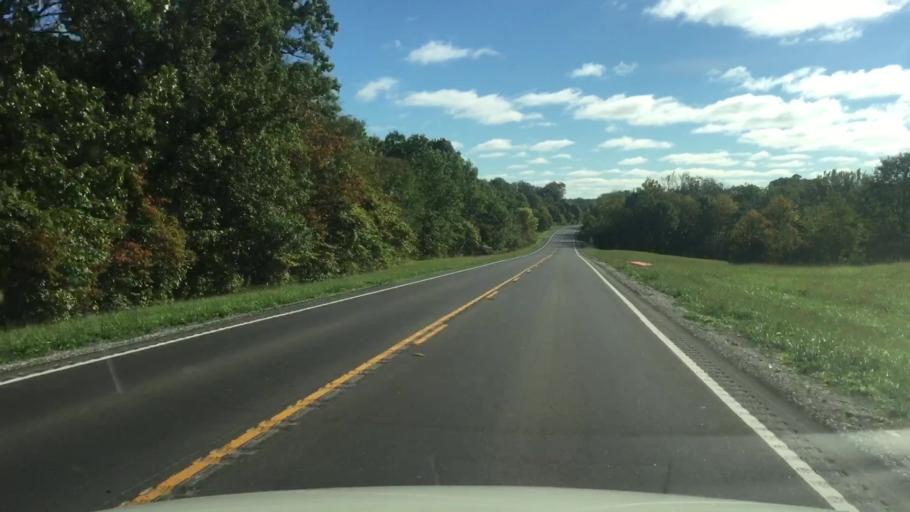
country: US
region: Missouri
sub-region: Howard County
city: New Franklin
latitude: 38.9974
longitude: -92.5880
